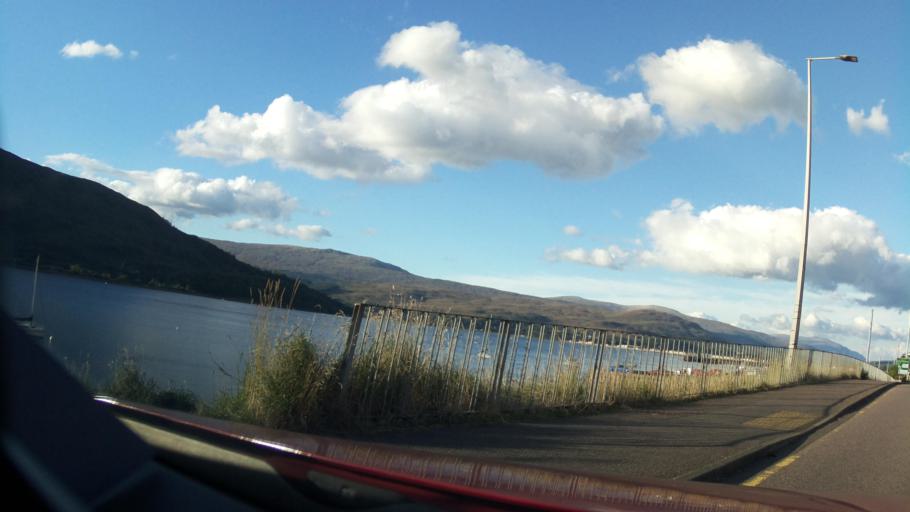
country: GB
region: Scotland
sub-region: Highland
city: Fort William
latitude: 56.8139
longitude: -5.1204
